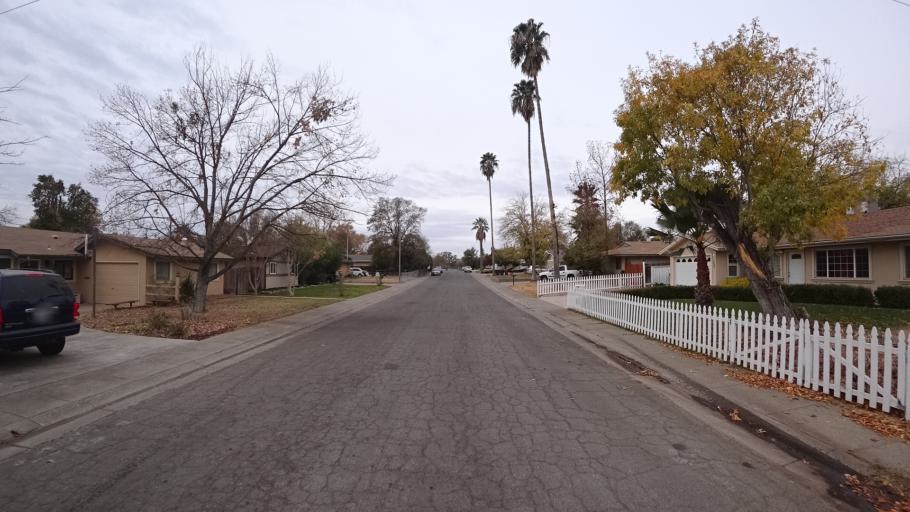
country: US
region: California
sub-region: Sacramento County
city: Citrus Heights
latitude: 38.7120
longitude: -121.2929
